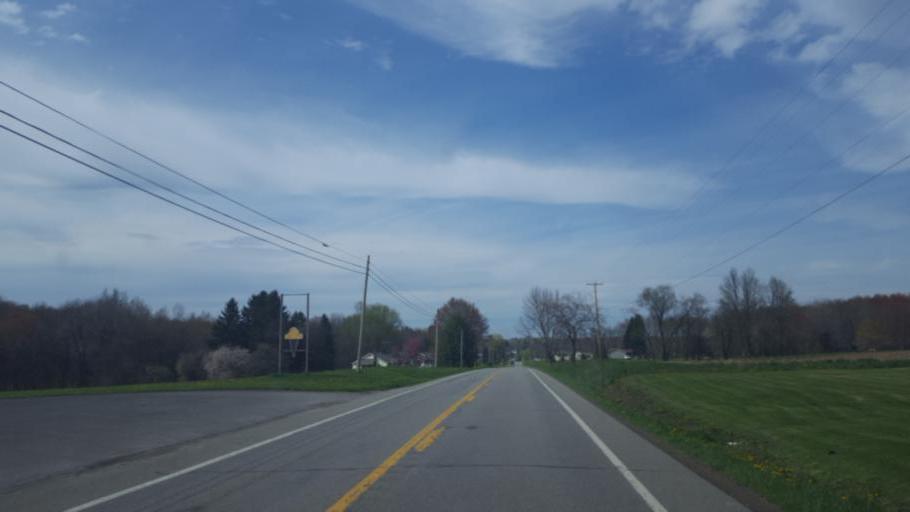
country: US
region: Pennsylvania
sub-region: Mercer County
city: Stoneboro
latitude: 41.3994
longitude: -80.0739
